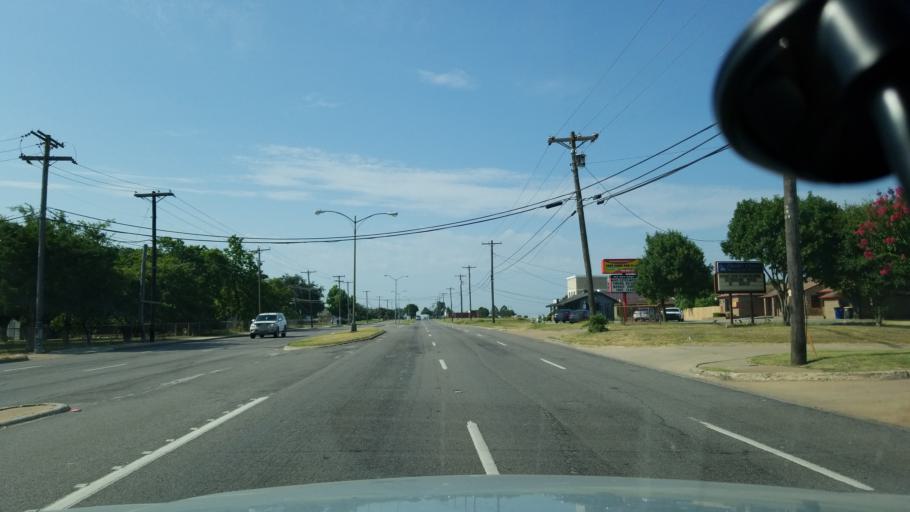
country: US
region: Texas
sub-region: Dallas County
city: Cockrell Hill
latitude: 32.6896
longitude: -96.8572
